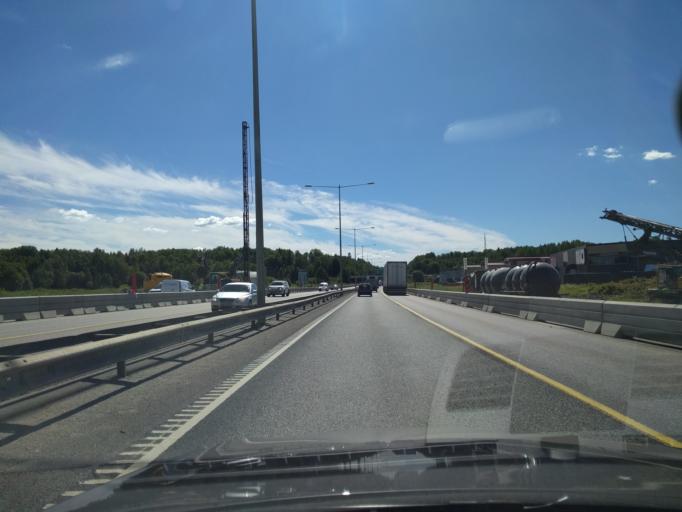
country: SE
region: Stockholm
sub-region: Haninge Kommun
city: Haninge
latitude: 59.1876
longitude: 18.1477
